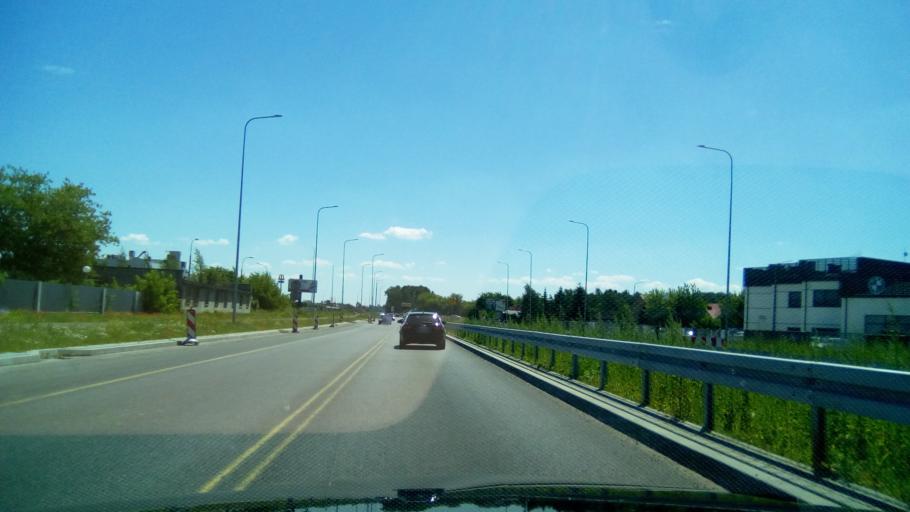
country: PL
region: Masovian Voivodeship
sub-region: Radom
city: Radom
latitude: 51.4163
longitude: 21.1968
